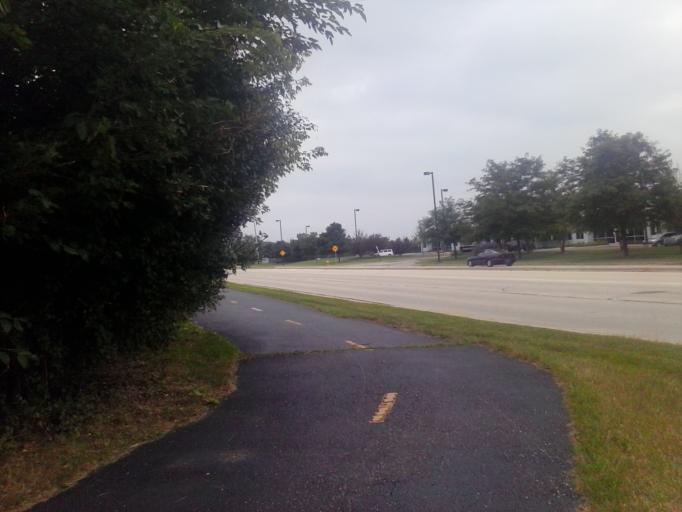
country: US
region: Illinois
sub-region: Cook County
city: Lemont
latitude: 41.7032
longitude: -88.0212
